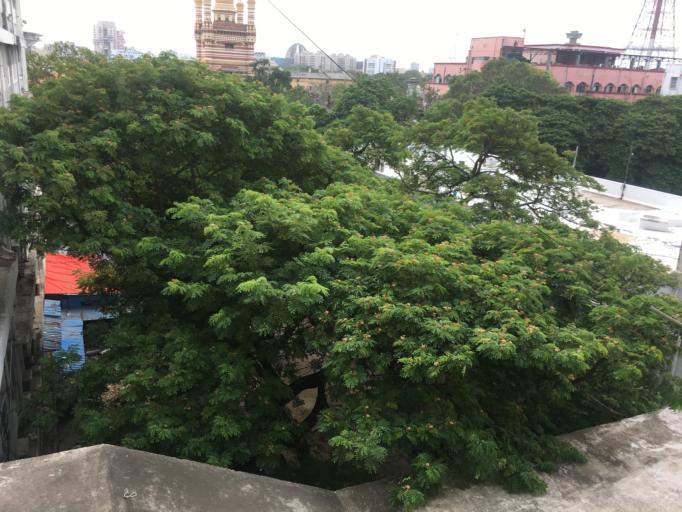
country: IN
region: Tamil Nadu
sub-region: Chennai
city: Chennai
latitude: 13.0633
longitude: 80.2825
